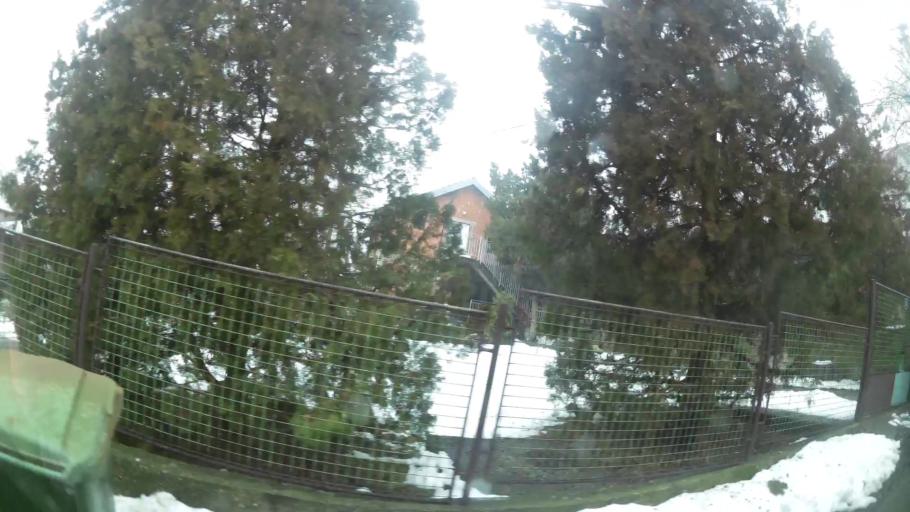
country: RS
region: Central Serbia
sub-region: Belgrade
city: Zvezdara
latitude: 44.7731
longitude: 20.5257
